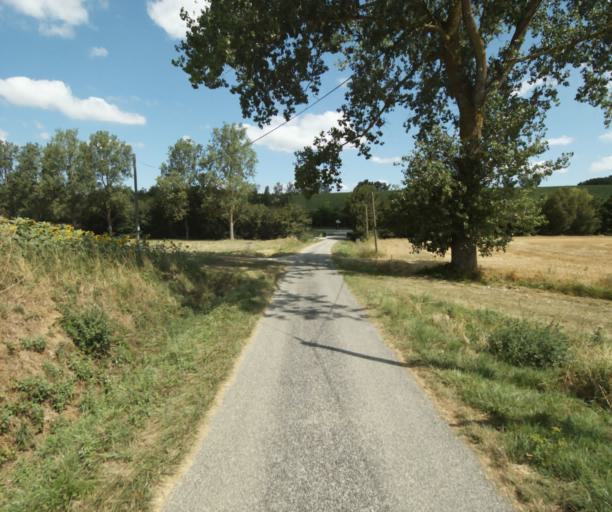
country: FR
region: Midi-Pyrenees
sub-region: Departement de la Haute-Garonne
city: Auriac-sur-Vendinelle
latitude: 43.4798
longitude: 1.7962
